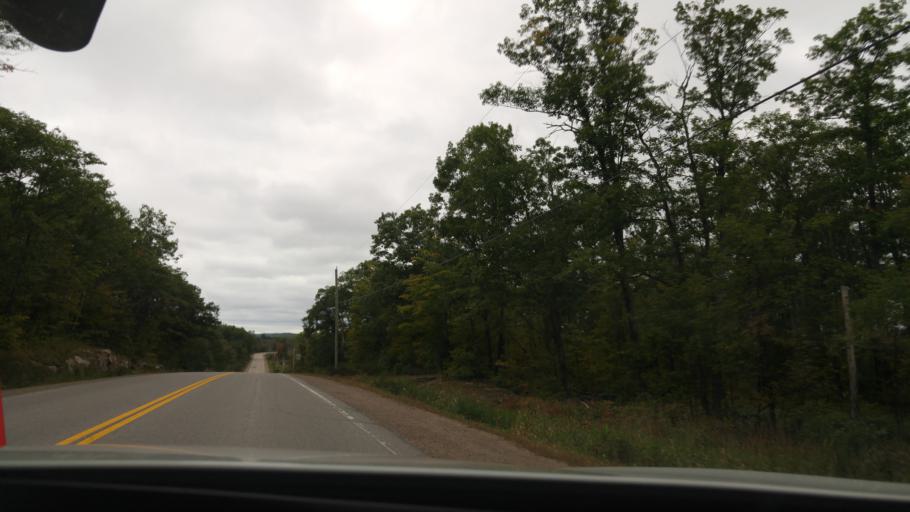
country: CA
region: Ontario
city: Petawawa
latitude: 45.8207
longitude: -77.3052
